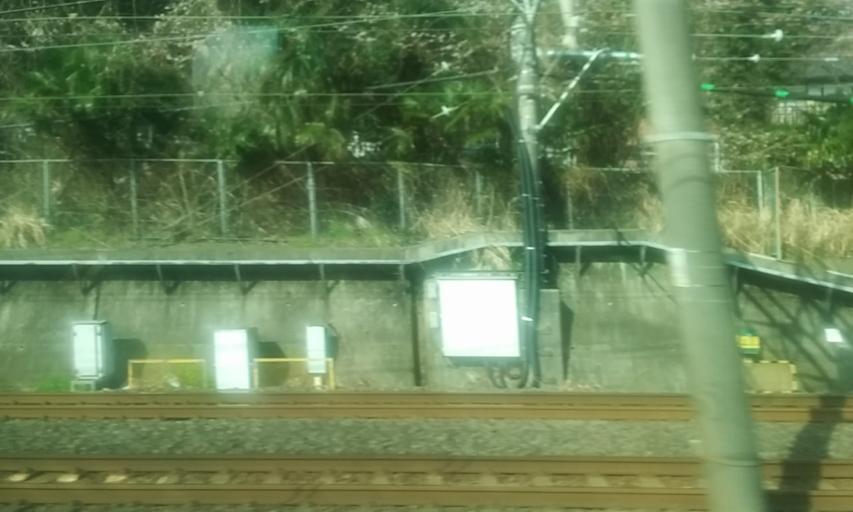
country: JP
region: Kanagawa
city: Yokohama
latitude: 35.4339
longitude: 139.5564
